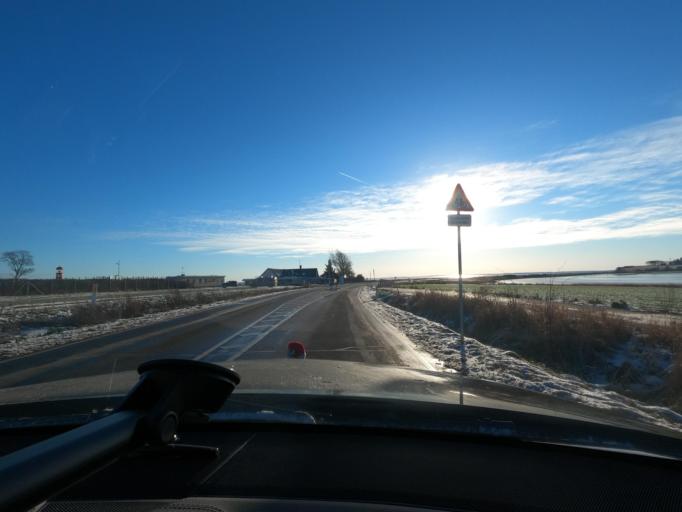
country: DE
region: Schleswig-Holstein
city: Pommerby
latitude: 54.8616
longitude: 9.9986
